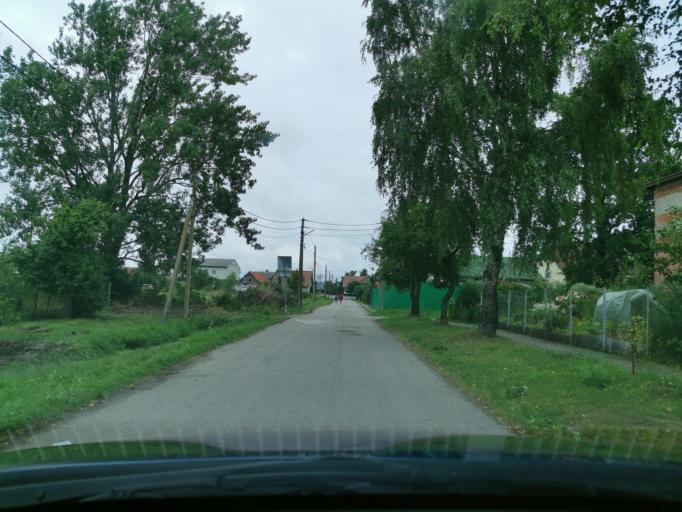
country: LT
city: Nida
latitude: 55.1529
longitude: 20.8524
